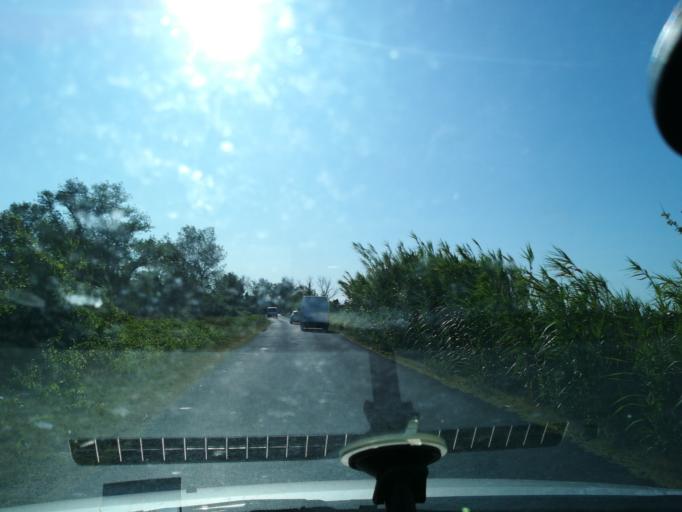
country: FR
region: Languedoc-Roussillon
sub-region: Departement de l'Herault
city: Vias
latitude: 43.2911
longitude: 3.3854
